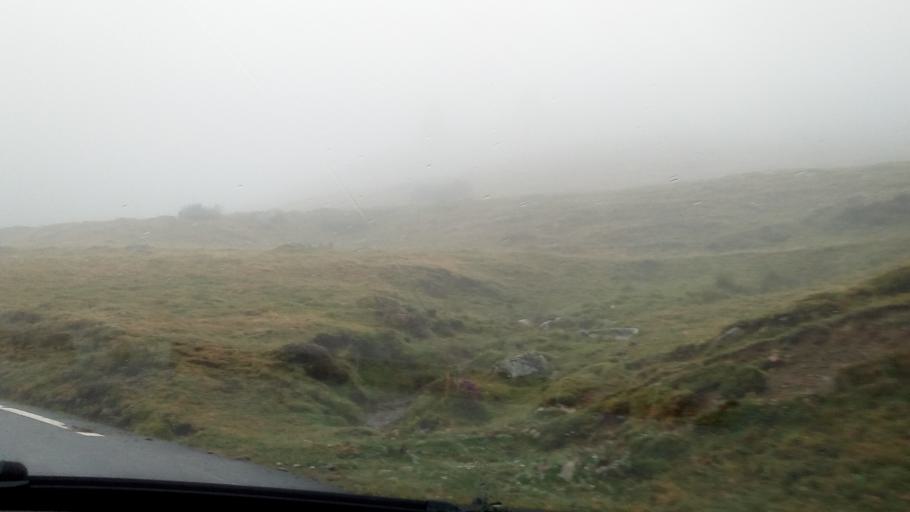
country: FR
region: Midi-Pyrenees
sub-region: Departement des Hautes-Pyrenees
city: Luz-Saint-Sauveur
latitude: 42.9072
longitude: 0.1163
